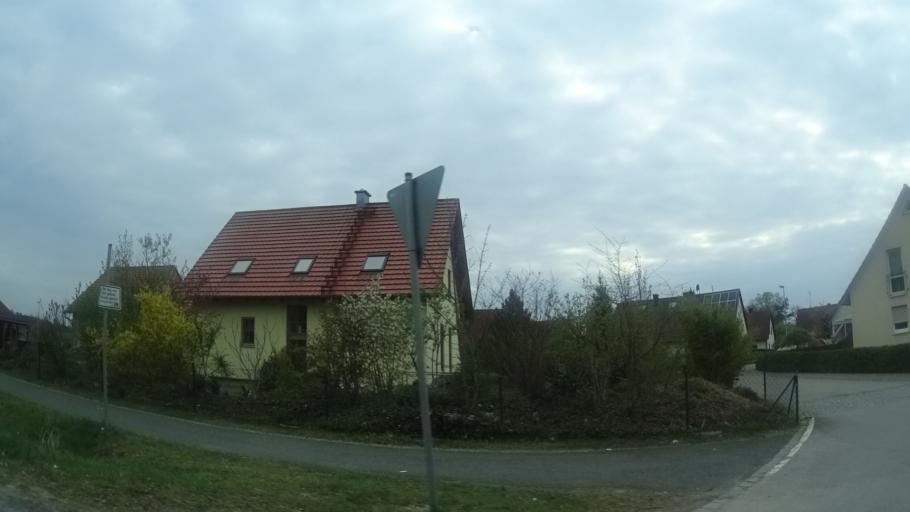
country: DE
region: Bavaria
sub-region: Regierungsbezirk Mittelfranken
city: Schnaittach
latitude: 49.5689
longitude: 11.3146
